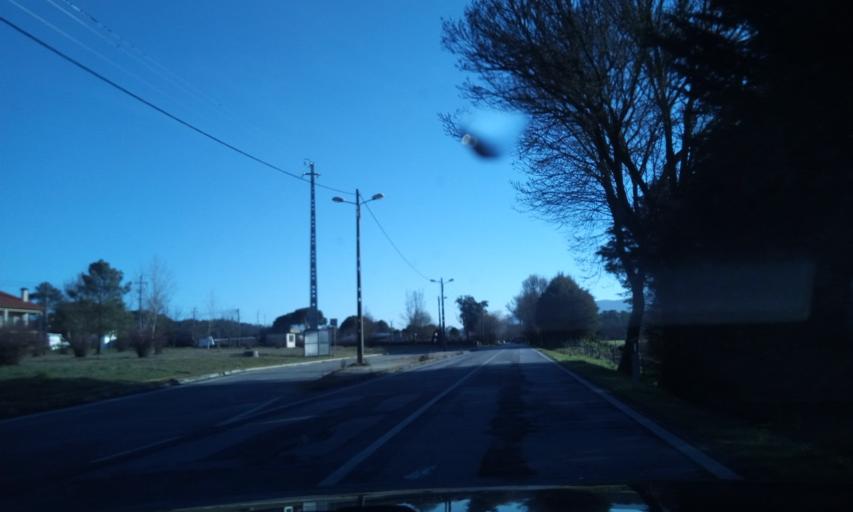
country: PT
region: Guarda
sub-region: Seia
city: Seia
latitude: 40.4528
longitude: -7.7048
